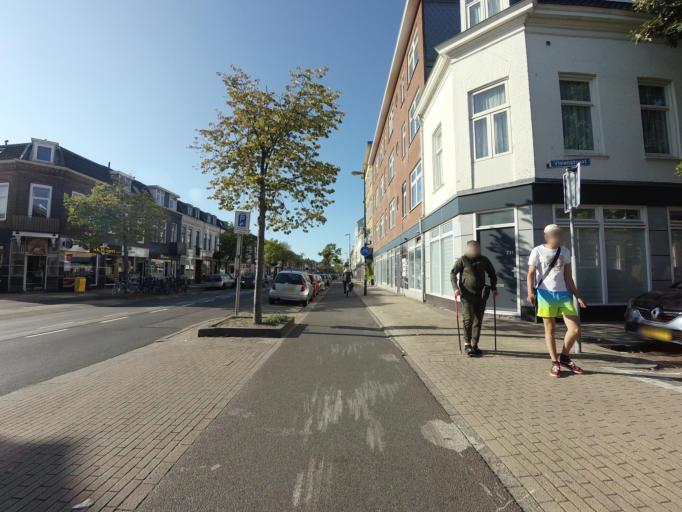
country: NL
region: Utrecht
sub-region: Gemeente Utrecht
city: Utrecht
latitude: 52.1000
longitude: 5.1014
